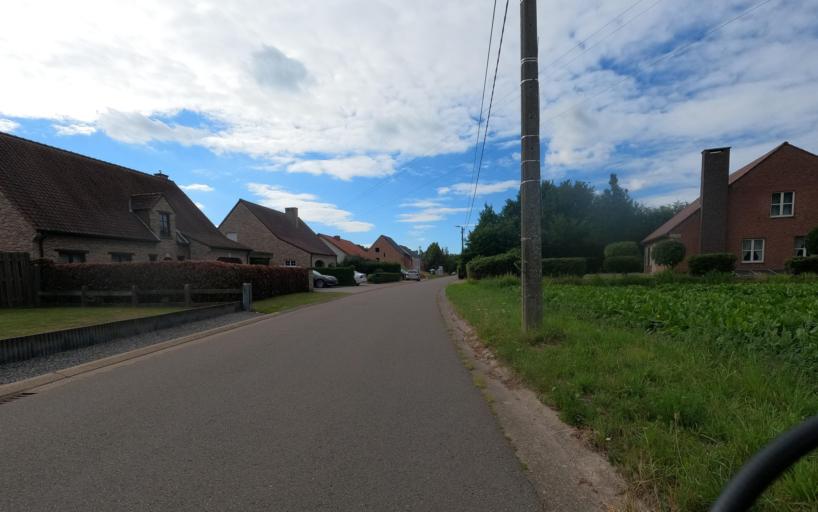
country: BE
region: Flanders
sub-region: Provincie Vlaams-Brabant
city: Begijnendijk
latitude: 51.0178
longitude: 4.7513
